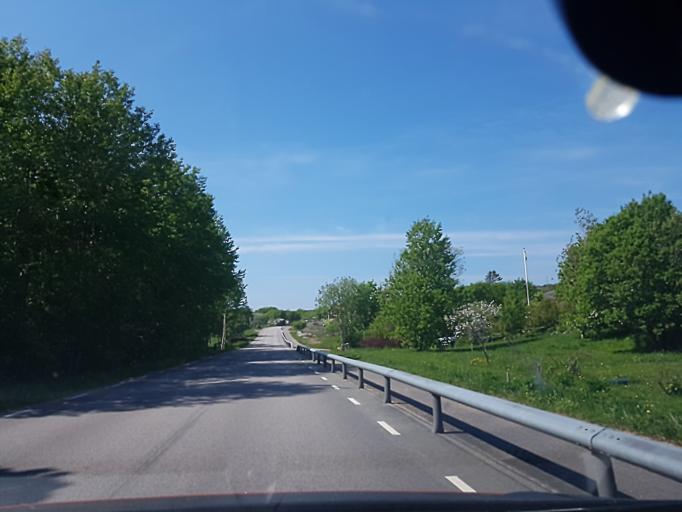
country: SE
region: Vaestra Goetaland
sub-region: Lysekils Kommun
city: Lysekil
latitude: 58.1658
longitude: 11.4382
